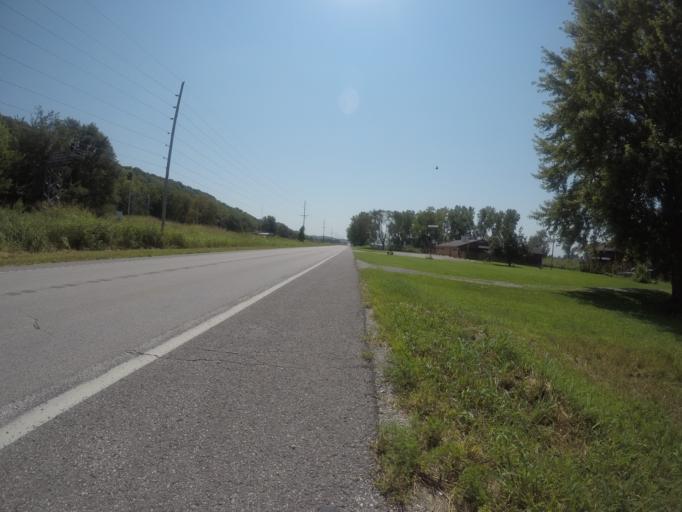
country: US
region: Kansas
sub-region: Atchison County
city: Atchison
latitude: 39.5315
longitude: -95.0363
